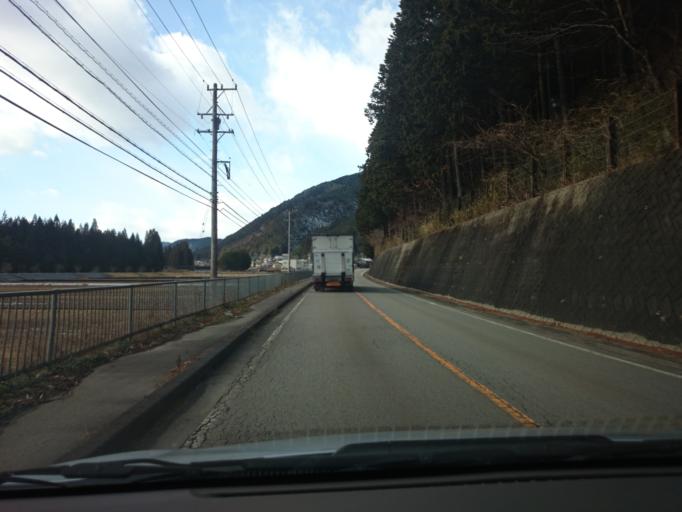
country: JP
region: Gifu
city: Gujo
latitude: 35.7528
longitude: 137.0953
